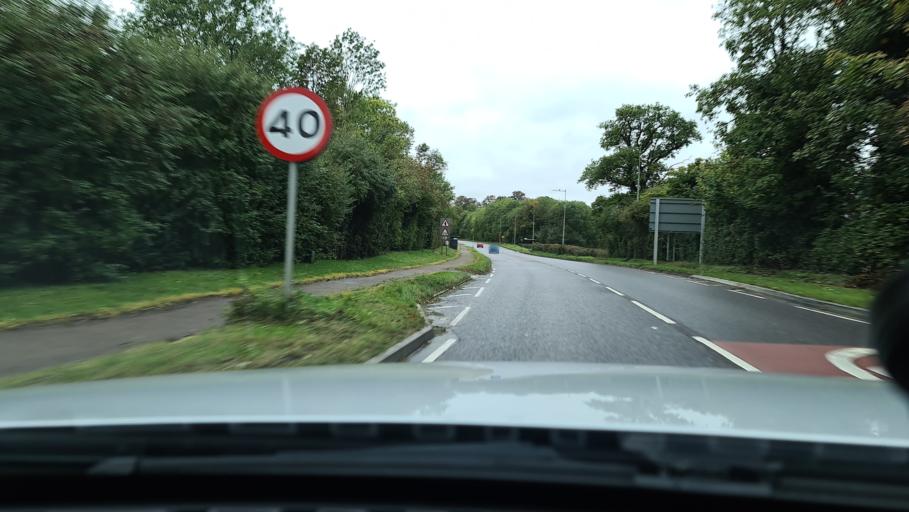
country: GB
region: England
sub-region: Milton Keynes
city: Stony Stratford
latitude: 52.0616
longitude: -0.8316
